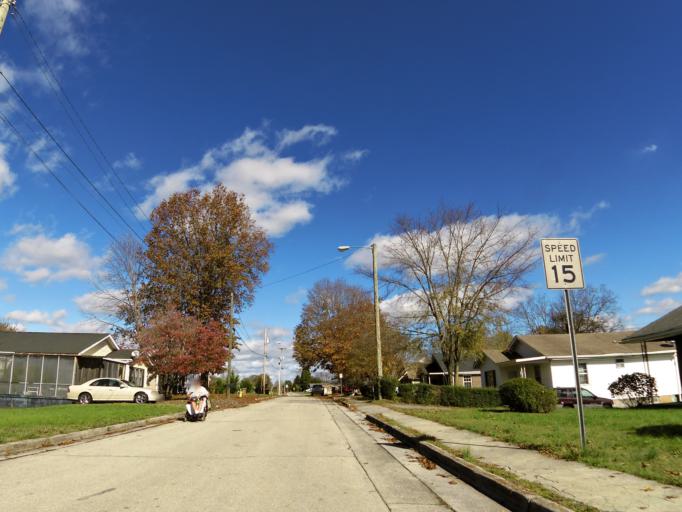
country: US
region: Tennessee
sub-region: Blount County
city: Alcoa
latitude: 35.7793
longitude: -83.9845
